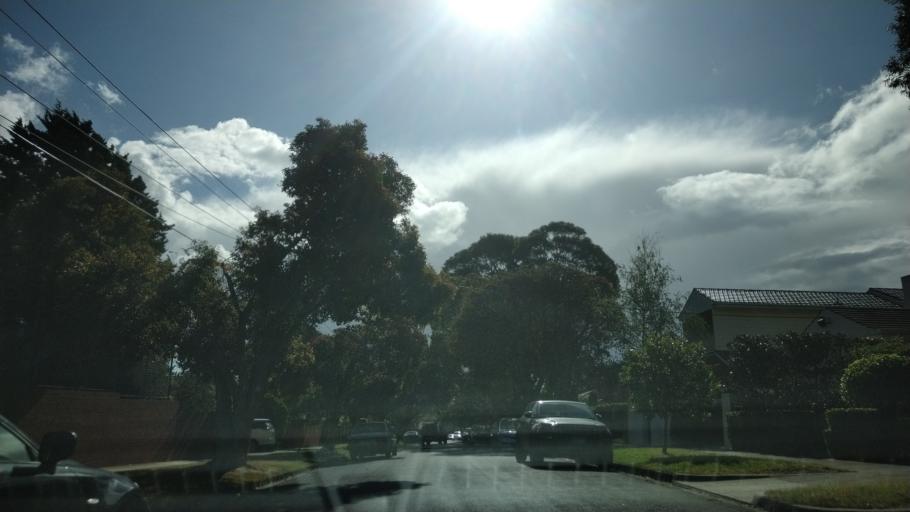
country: AU
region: Victoria
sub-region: Glen Eira
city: Caulfield South
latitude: -37.8916
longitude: 145.0196
